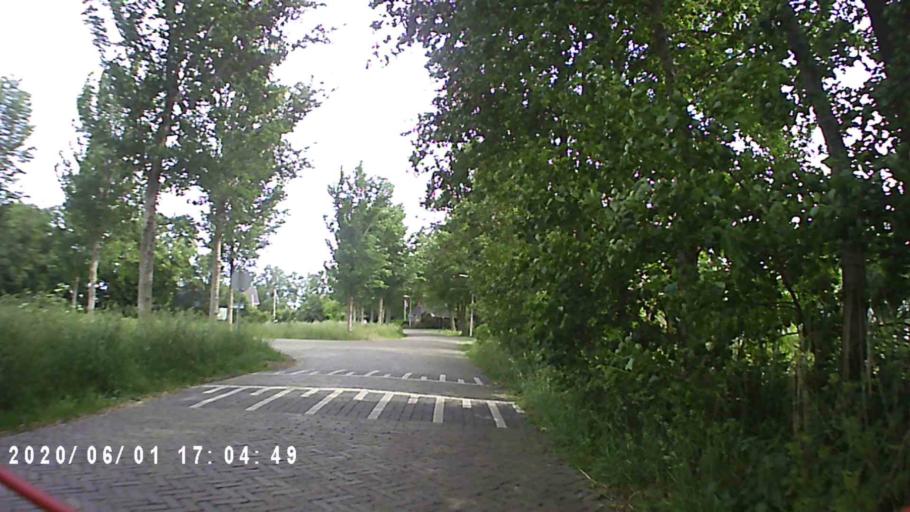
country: NL
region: Friesland
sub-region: Gemeente Tytsjerksteradiel
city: Garyp
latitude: 53.1731
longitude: 5.9338
